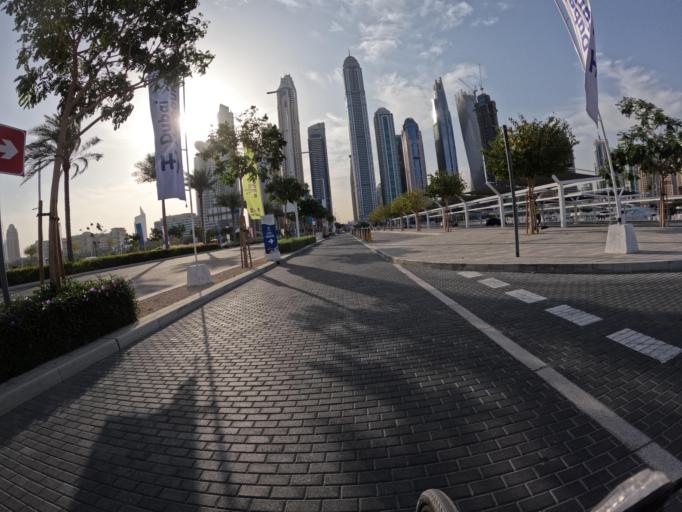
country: AE
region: Dubai
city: Dubai
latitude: 25.0928
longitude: 55.1426
